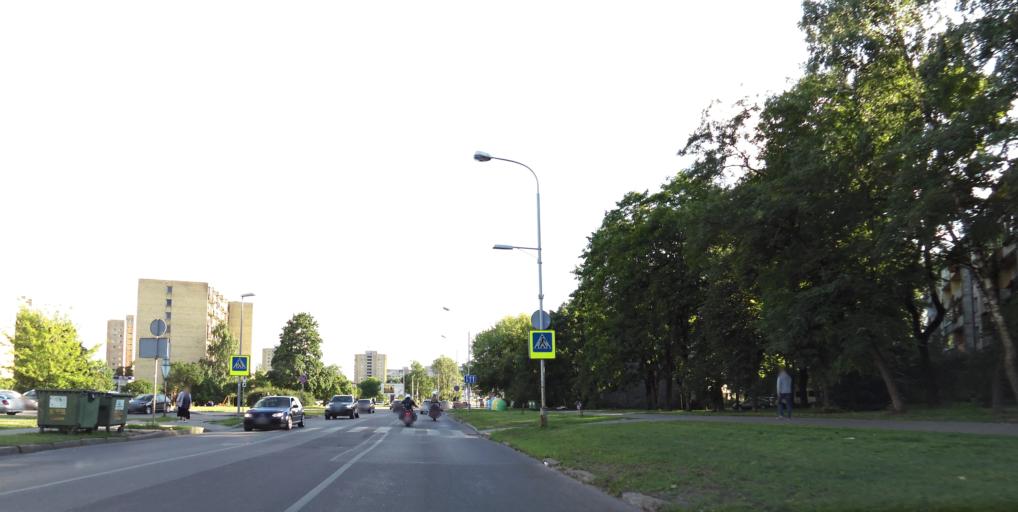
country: LT
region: Vilnius County
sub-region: Vilnius
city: Vilnius
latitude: 54.7055
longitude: 25.2897
